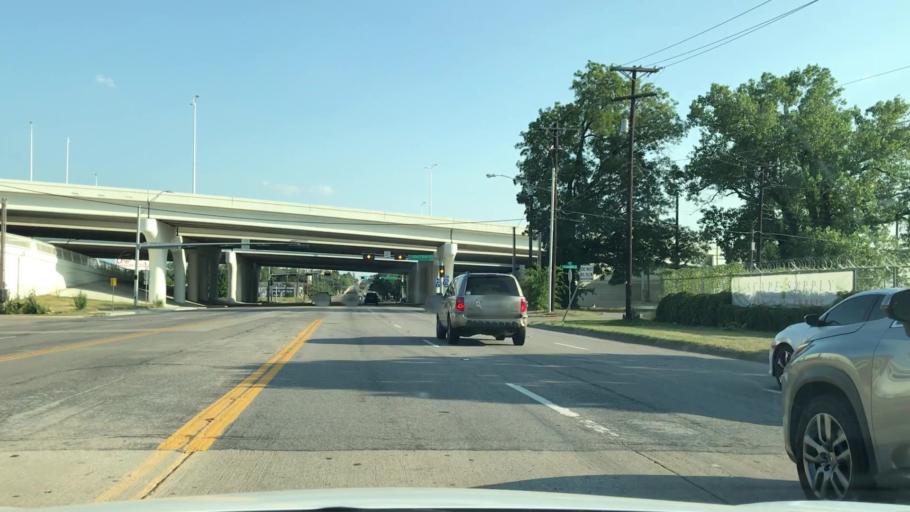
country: US
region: Texas
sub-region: Dallas County
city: Dallas
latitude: 32.7704
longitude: -96.8229
